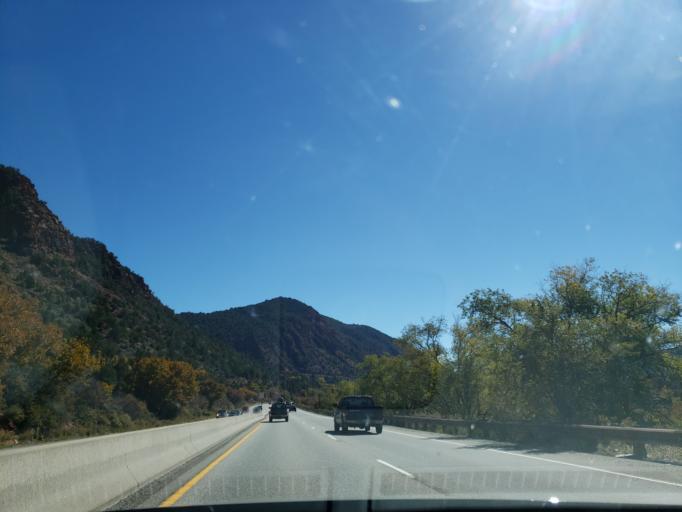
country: US
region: Colorado
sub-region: Garfield County
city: Glenwood Springs
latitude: 39.5120
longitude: -107.3080
